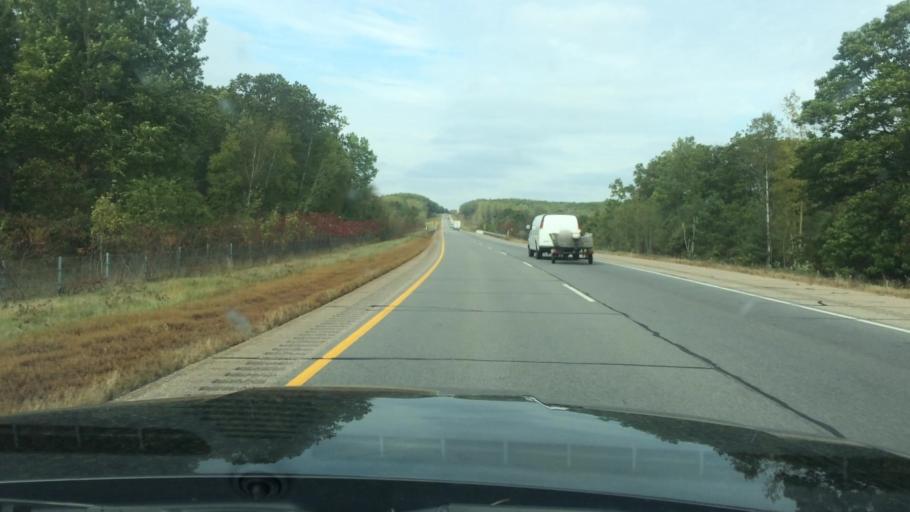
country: US
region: Wisconsin
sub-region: Marathon County
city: Mosinee
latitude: 44.6930
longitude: -89.6427
